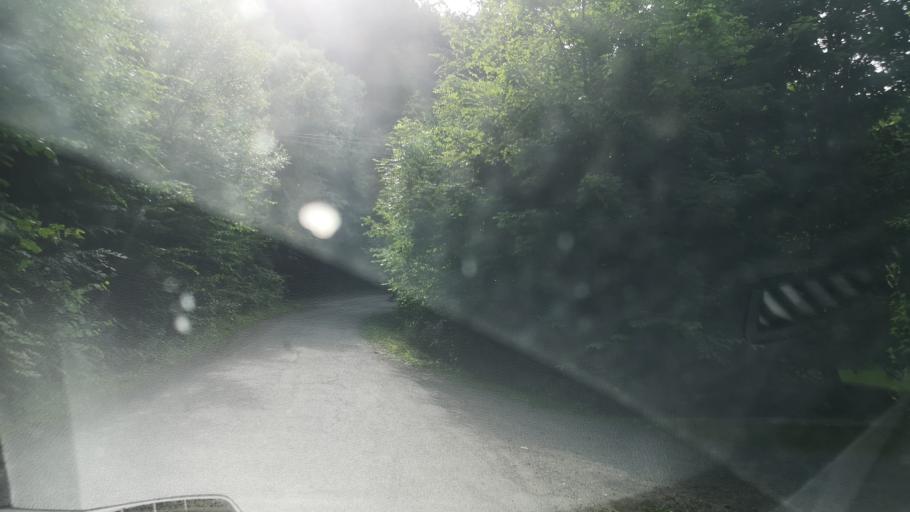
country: SK
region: Banskobystricky
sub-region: Okres Banska Bystrica
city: Banska Stiavnica
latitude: 48.4612
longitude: 18.8538
